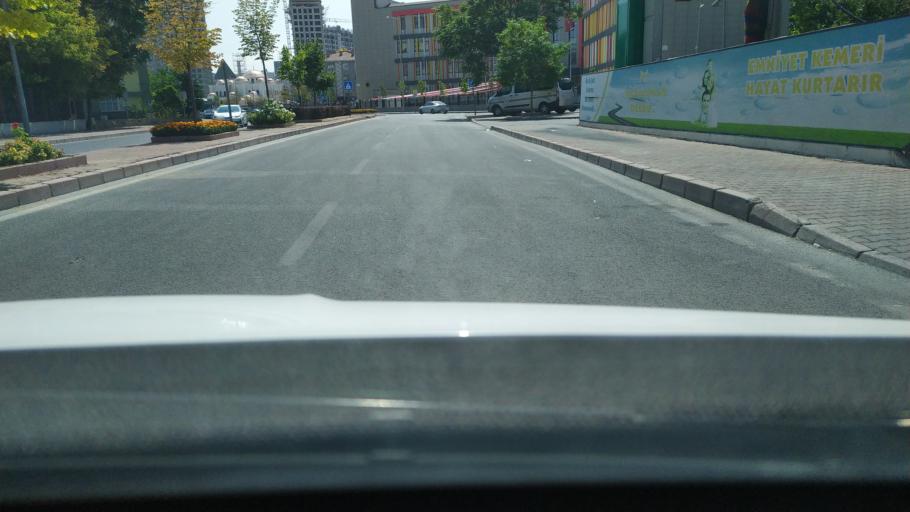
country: TR
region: Kayseri
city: Kayseri
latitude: 38.7313
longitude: 35.4870
